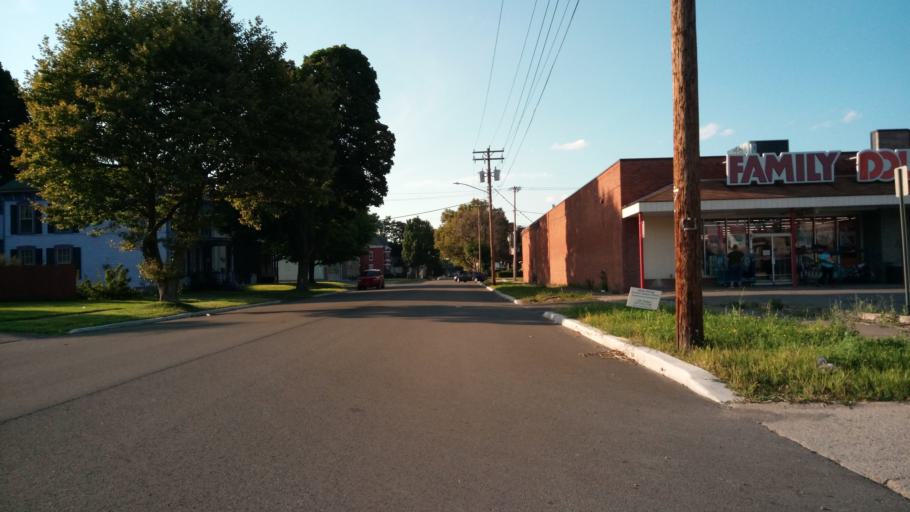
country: US
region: New York
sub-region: Chemung County
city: Elmira
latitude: 42.0925
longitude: -76.8014
